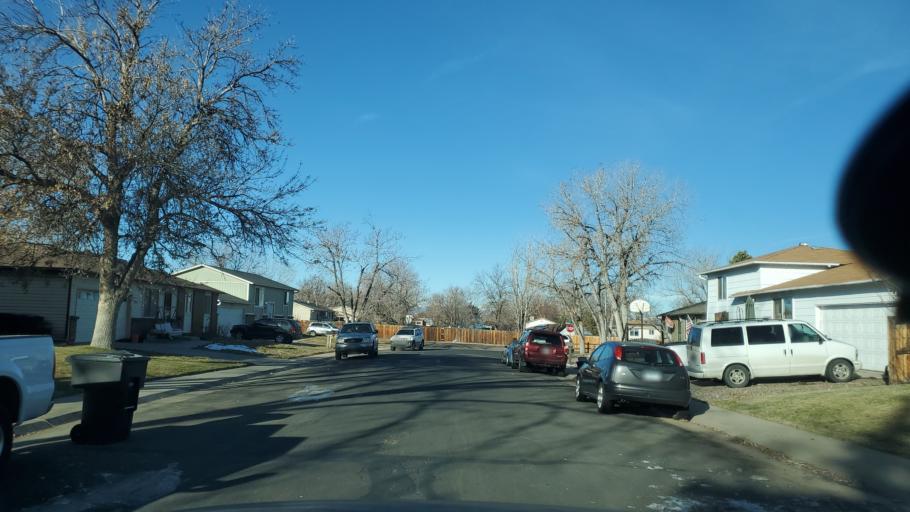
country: US
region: Colorado
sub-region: Adams County
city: Northglenn
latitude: 39.9110
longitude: -104.9453
